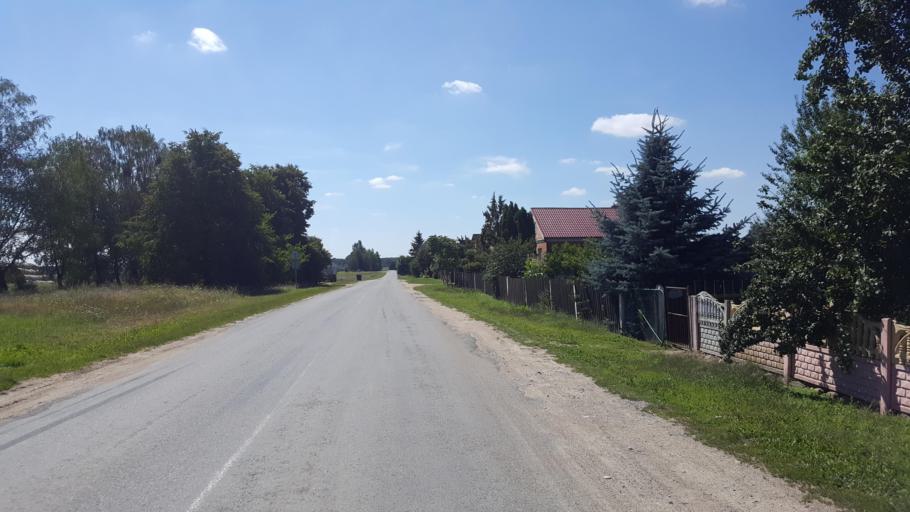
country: BY
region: Brest
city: Charnawchytsy
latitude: 52.3438
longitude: 23.6064
